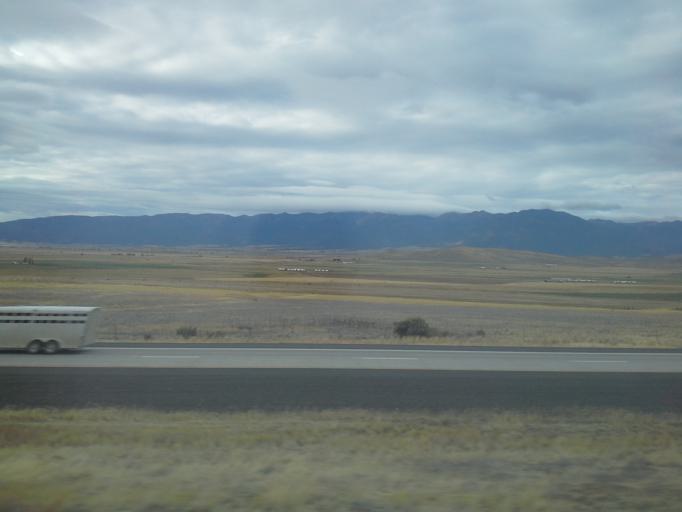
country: US
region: Oregon
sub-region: Baker County
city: Baker City
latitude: 44.9236
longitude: -117.8256
